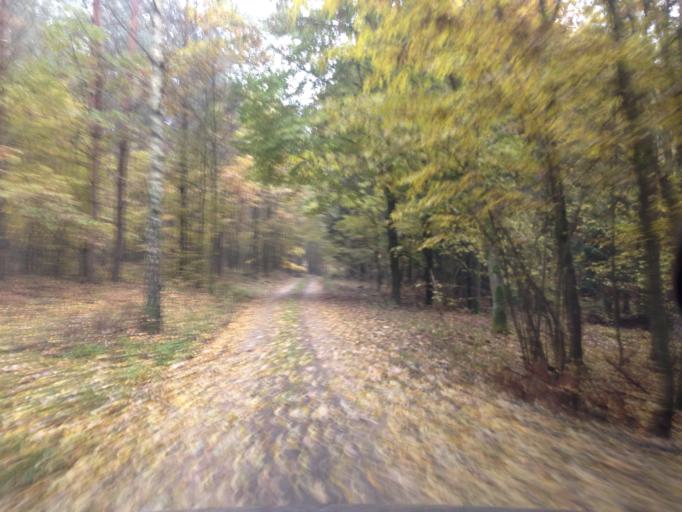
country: PL
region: Kujawsko-Pomorskie
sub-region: Powiat brodnicki
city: Gorzno
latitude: 53.2225
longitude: 19.7167
